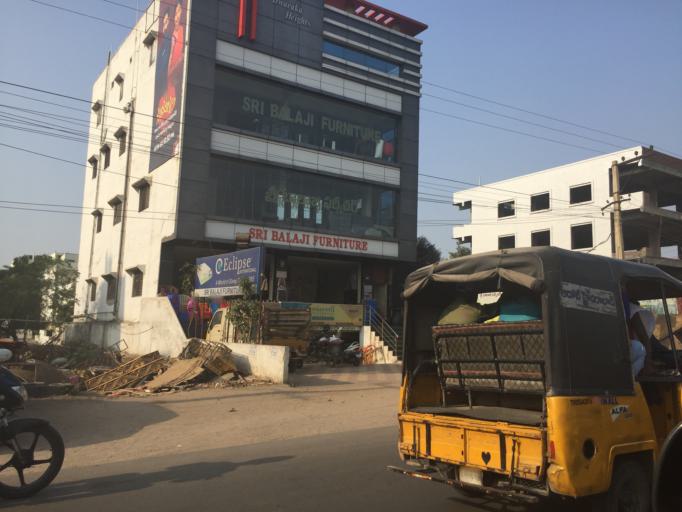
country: IN
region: Telangana
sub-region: Rangareddi
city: Uppal Kalan
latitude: 17.4034
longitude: 78.5838
